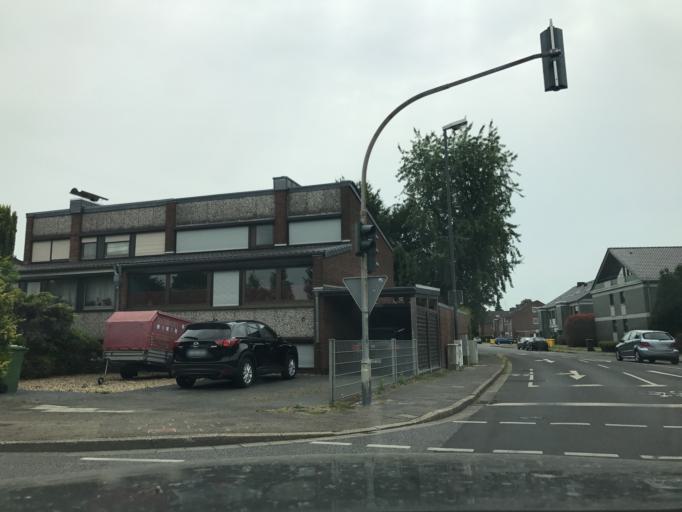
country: DE
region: North Rhine-Westphalia
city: Tonisvorst
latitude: 51.3277
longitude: 6.5007
